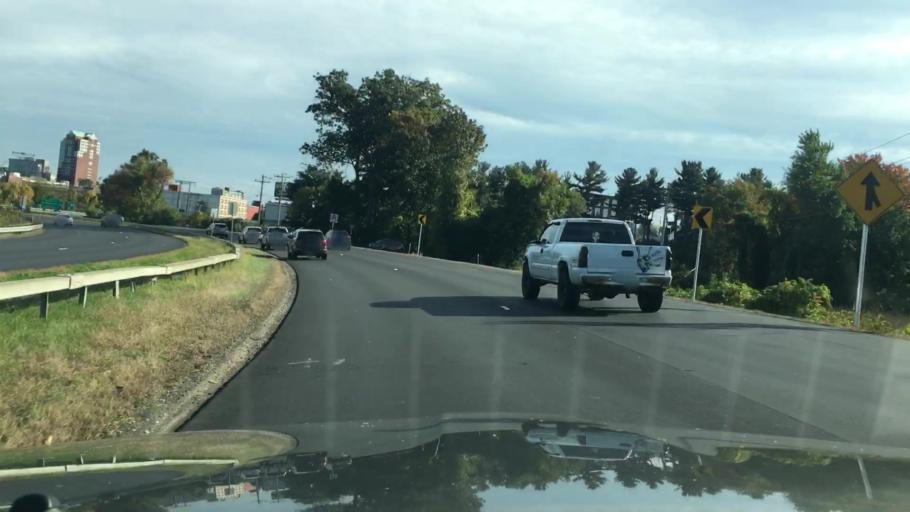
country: US
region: New Hampshire
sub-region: Hillsborough County
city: Manchester
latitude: 42.9990
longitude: -71.4747
